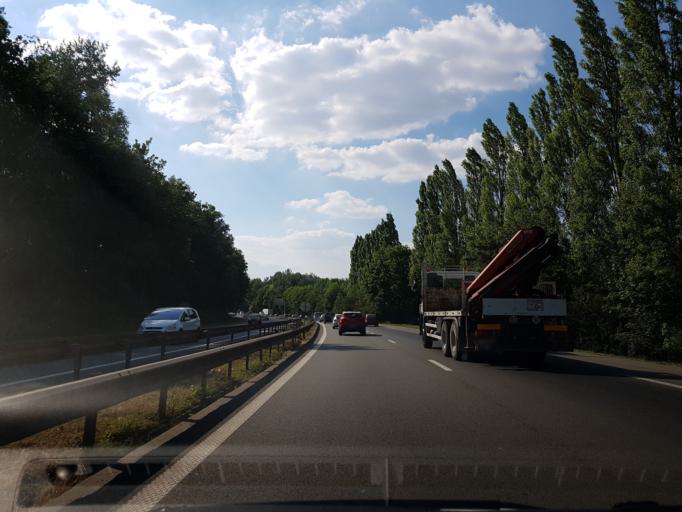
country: FR
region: Nord-Pas-de-Calais
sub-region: Departement du Pas-de-Calais
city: Courcelles-les-Lens
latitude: 50.4223
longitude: 3.0270
